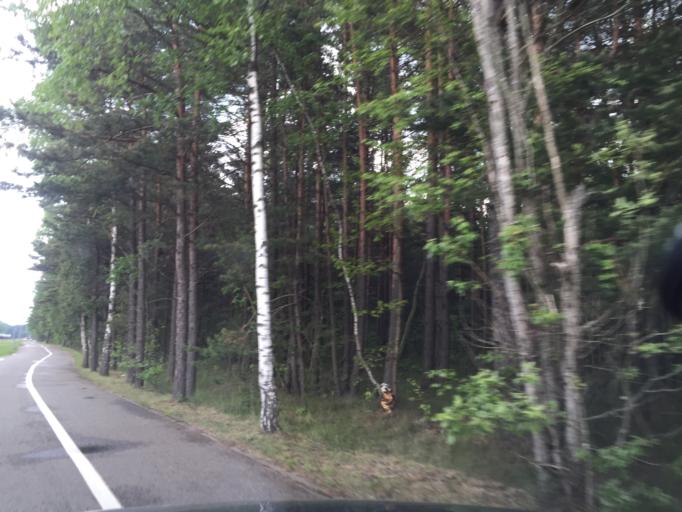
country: LT
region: Klaipedos apskritis
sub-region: Klaipeda
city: Klaipeda
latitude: 55.7639
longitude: 21.0961
